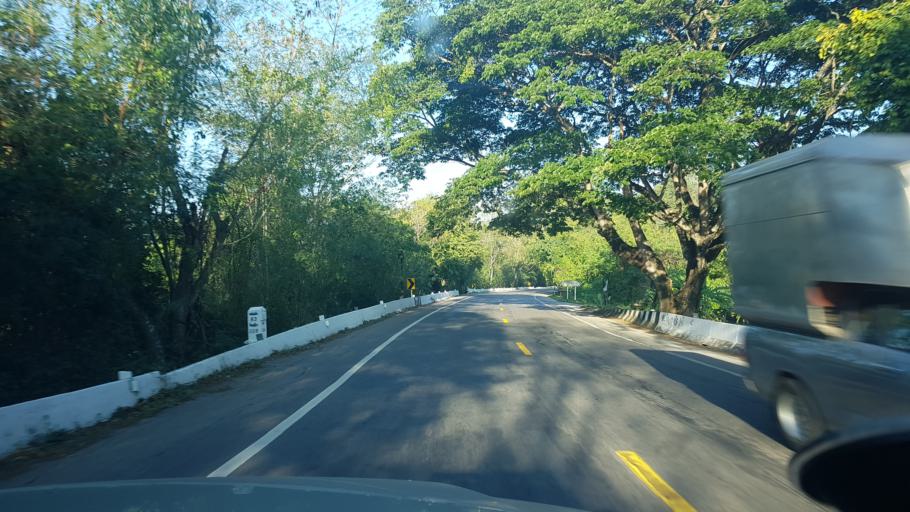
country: TH
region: Khon Kaen
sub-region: Amphoe Phu Pha Man
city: Phu Pha Man
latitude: 16.6477
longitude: 101.7795
